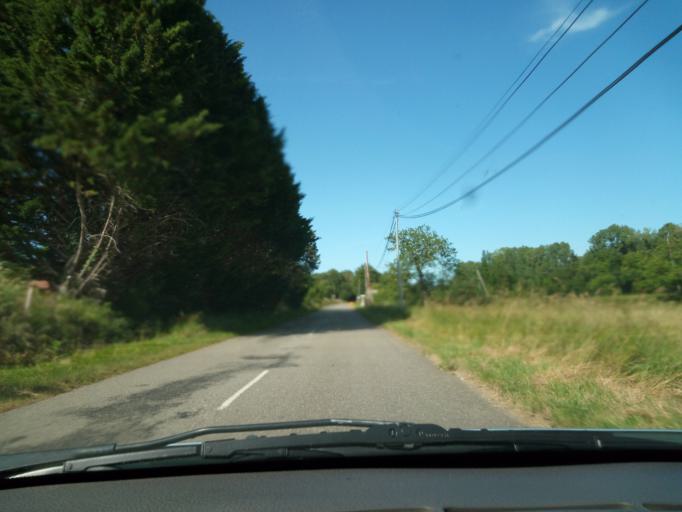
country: FR
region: Midi-Pyrenees
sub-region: Departement du Lot
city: Castelnau-Montratier
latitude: 44.2541
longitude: 1.3555
